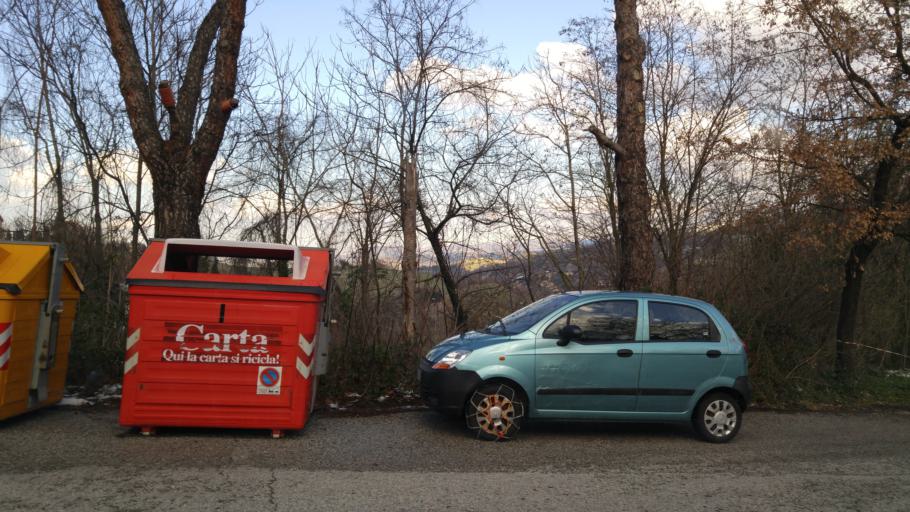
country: IT
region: The Marches
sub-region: Provincia di Pesaro e Urbino
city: Urbino
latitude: 43.7272
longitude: 12.6391
